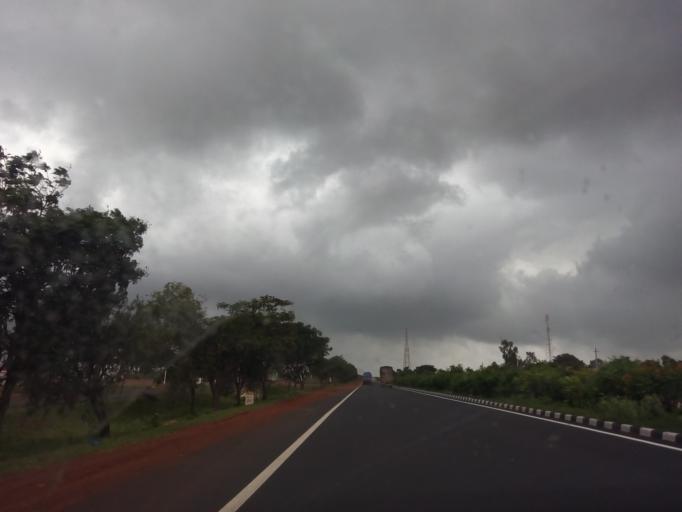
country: IN
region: Karnataka
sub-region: Belgaum
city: Belgaum
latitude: 16.0247
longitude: 74.5230
